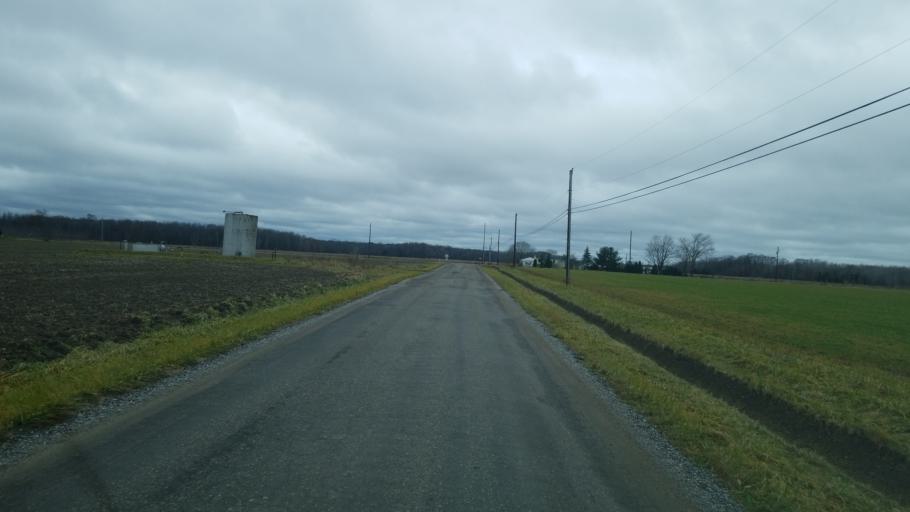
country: US
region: Ohio
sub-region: Ashtabula County
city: Jefferson
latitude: 41.7648
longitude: -80.6199
